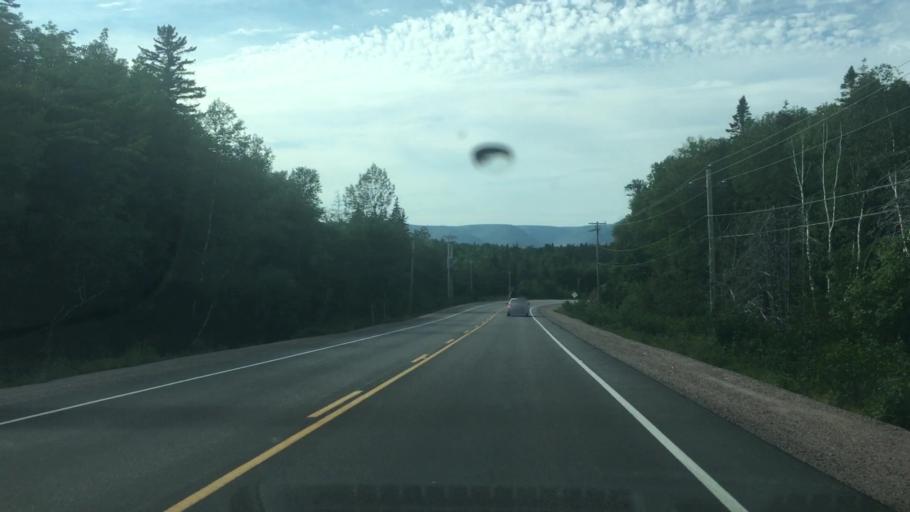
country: CA
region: Nova Scotia
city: Sydney Mines
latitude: 46.8569
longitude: -60.4606
